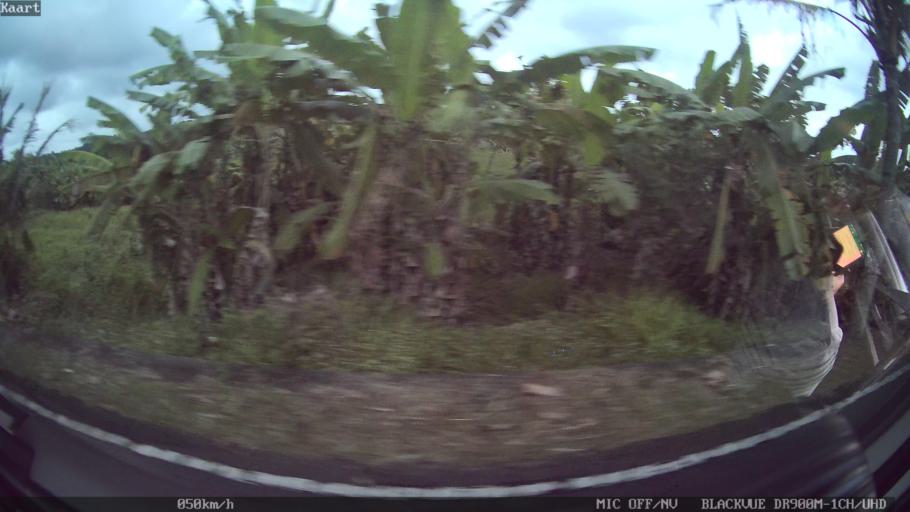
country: ID
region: Bali
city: Banjar Cemenggon
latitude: -8.5344
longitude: 115.1888
